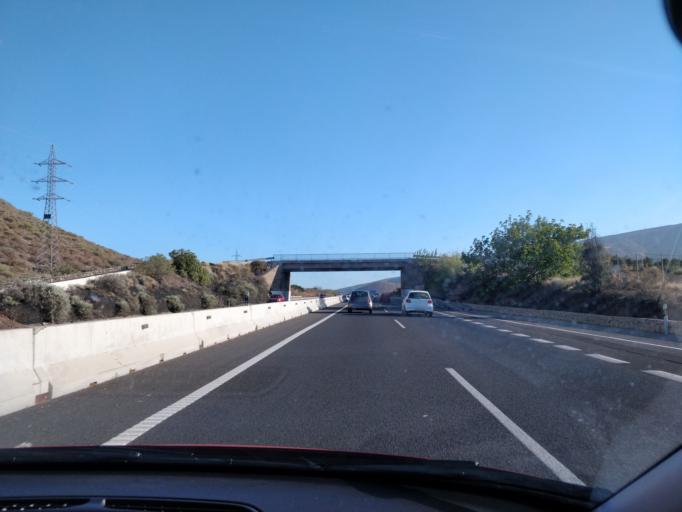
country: ES
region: Canary Islands
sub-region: Provincia de Santa Cruz de Tenerife
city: Candelaria
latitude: 28.3168
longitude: -16.3805
